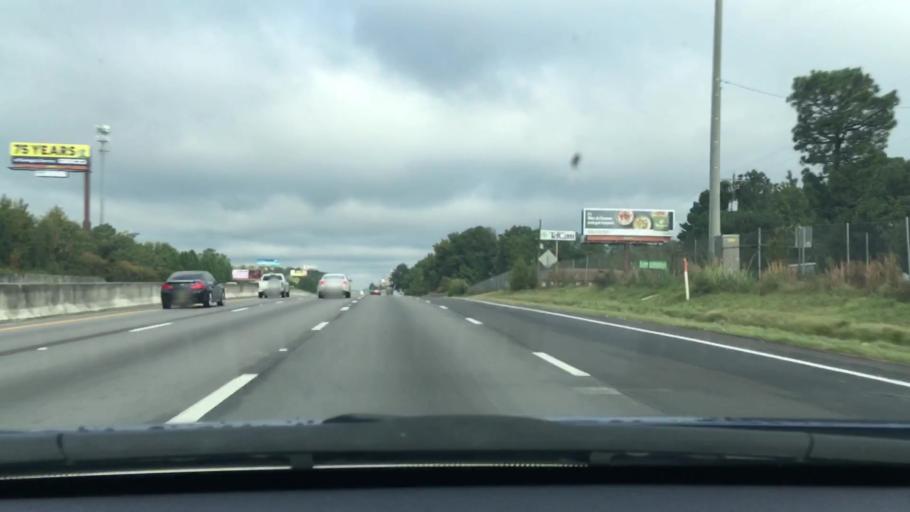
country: US
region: South Carolina
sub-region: Lexington County
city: Saint Andrews
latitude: 34.0470
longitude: -81.1201
